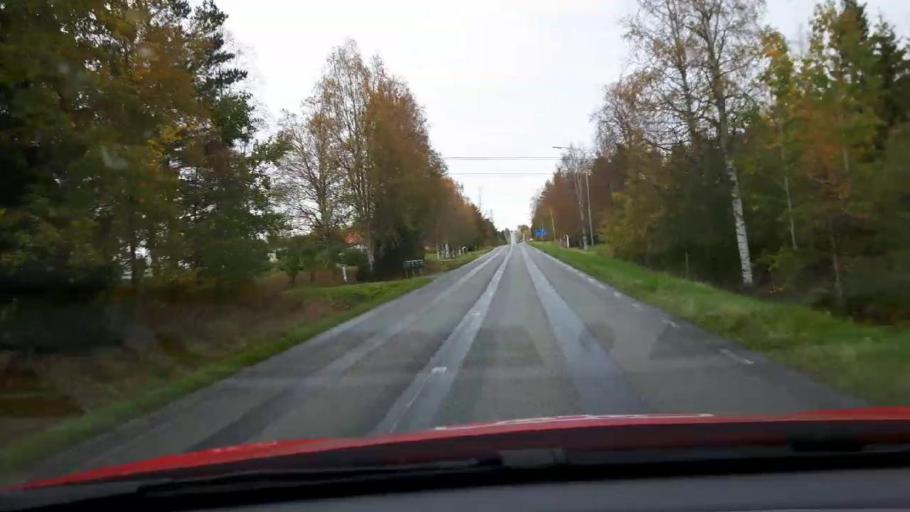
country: SE
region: Jaemtland
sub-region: Bergs Kommun
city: Hoverberg
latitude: 62.9948
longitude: 14.3395
